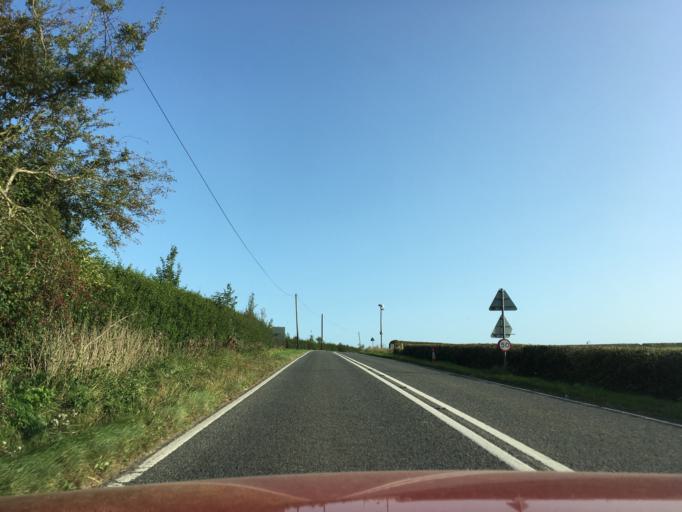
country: GB
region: England
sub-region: Gloucestershire
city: Gloucester
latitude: 51.9056
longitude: -2.2911
